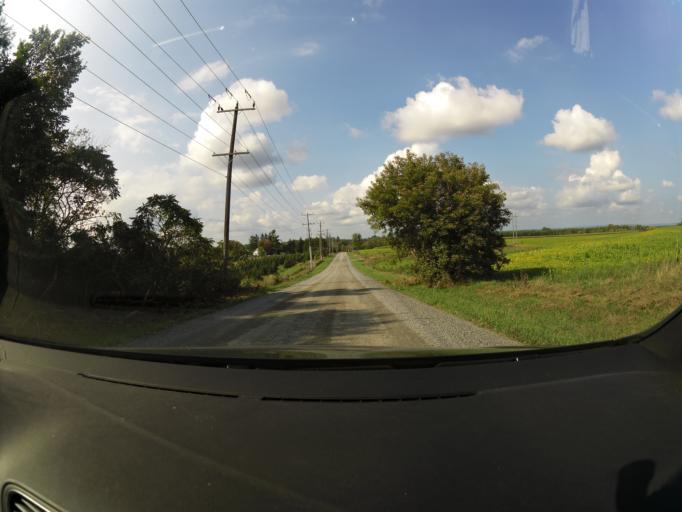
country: CA
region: Ontario
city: Arnprior
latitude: 45.4172
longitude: -76.2457
